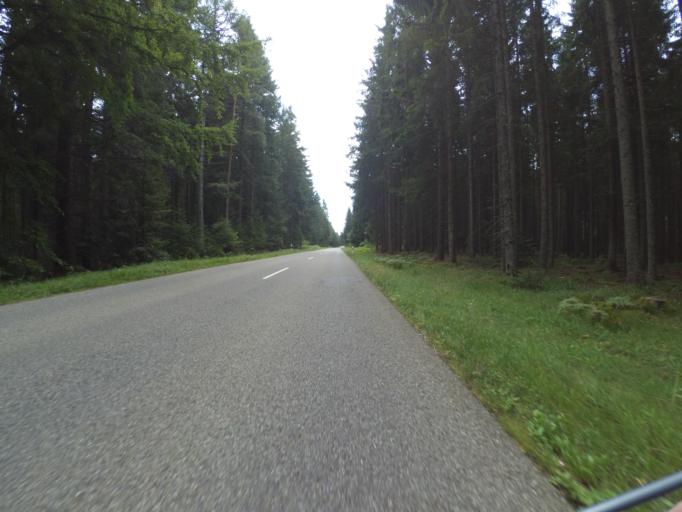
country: DE
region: Baden-Wuerttemberg
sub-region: Freiburg Region
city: Bonndorf im Schwarzwald
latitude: 47.8279
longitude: 8.2809
